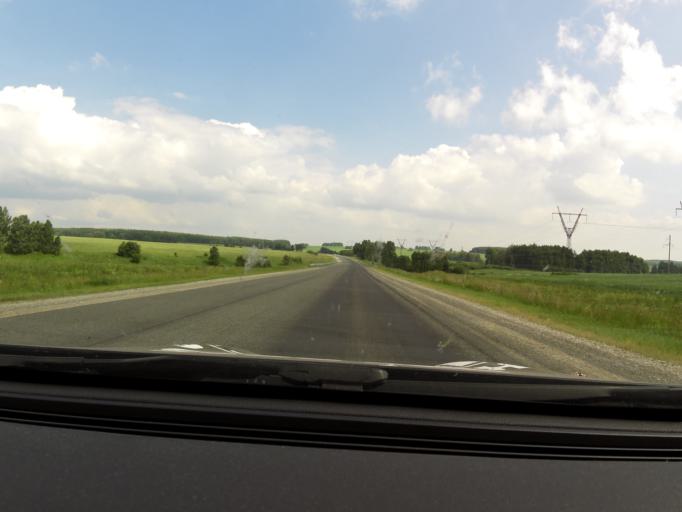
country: RU
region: Sverdlovsk
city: Ufimskiy
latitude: 56.7734
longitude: 58.0098
